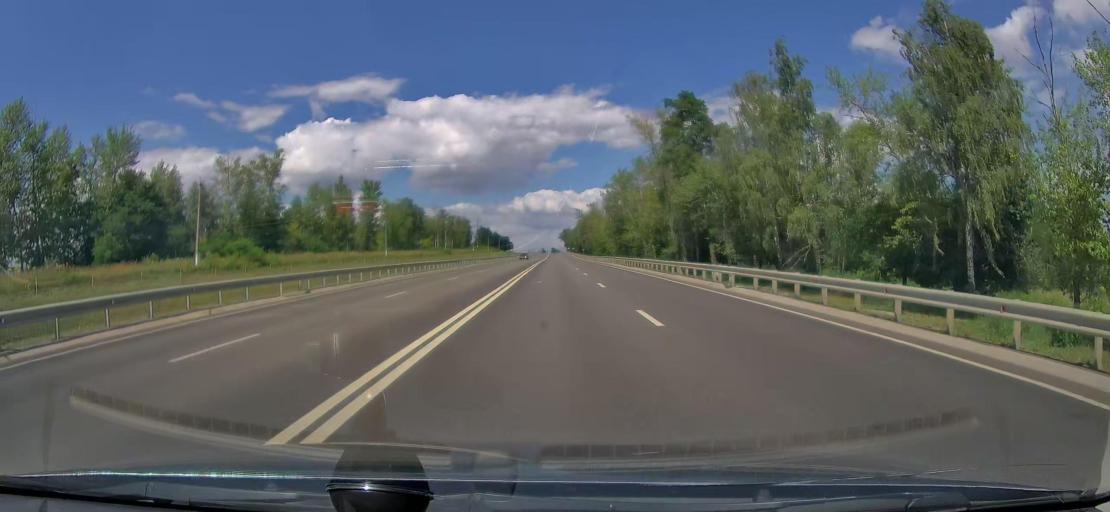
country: RU
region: Kursk
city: Zolotukhino
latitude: 51.9553
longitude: 36.3050
